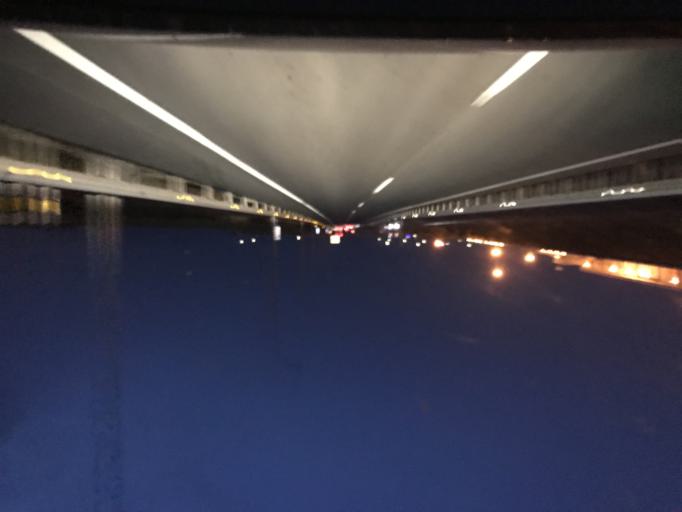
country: ES
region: Andalusia
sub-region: Provincia de Granada
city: Guadix
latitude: 37.3428
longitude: -3.0925
